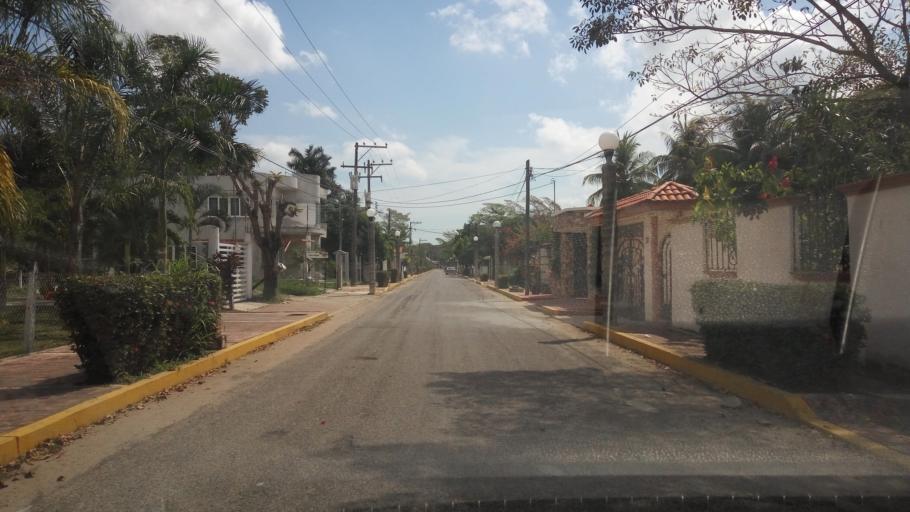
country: MX
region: Tabasco
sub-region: Comalcalco
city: Oriente 1ra. Seccion (Santo Domingo)
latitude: 18.2809
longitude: -93.2104
